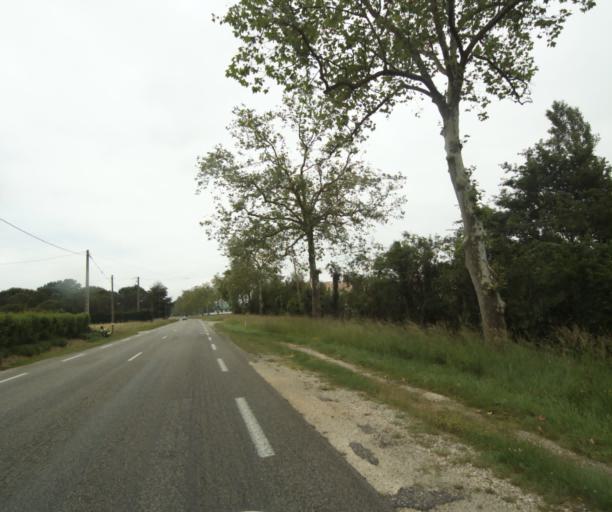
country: FR
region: Midi-Pyrenees
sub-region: Departement du Tarn-et-Garonne
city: Saint-Nauphary
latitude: 43.9758
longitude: 1.4072
